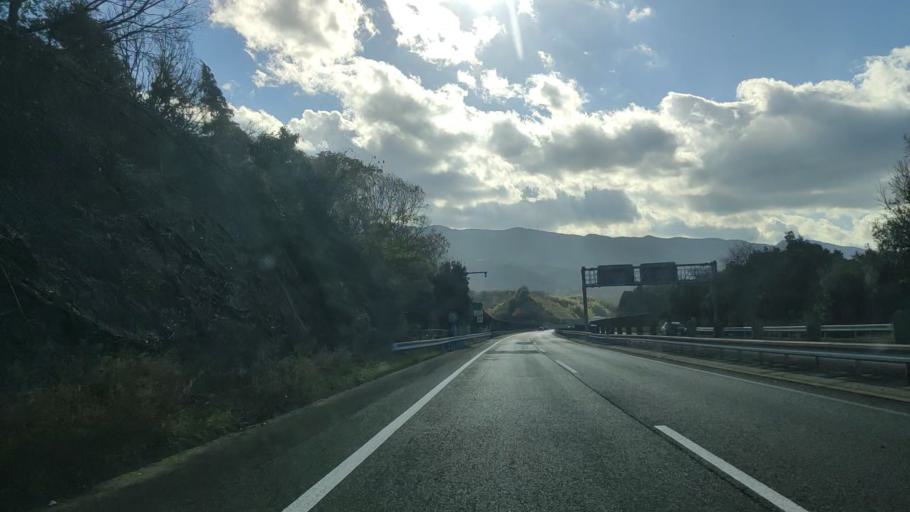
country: JP
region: Ehime
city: Kawanoecho
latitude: 33.9935
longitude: 133.5950
